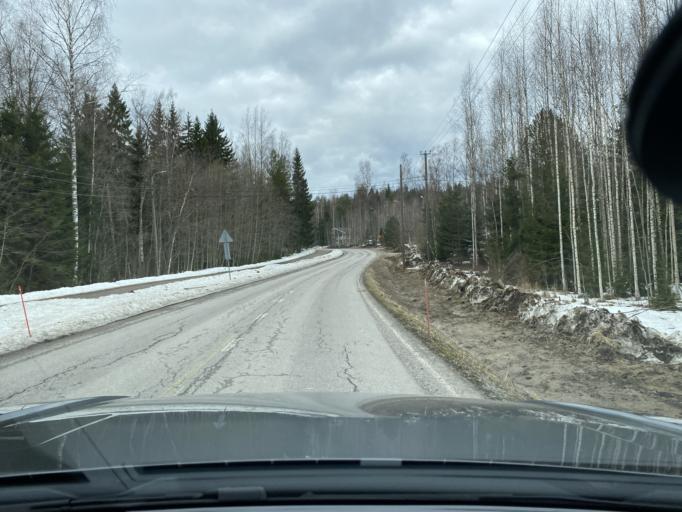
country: FI
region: Uusimaa
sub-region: Helsinki
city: Hyvinge
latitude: 60.5698
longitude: 24.7989
